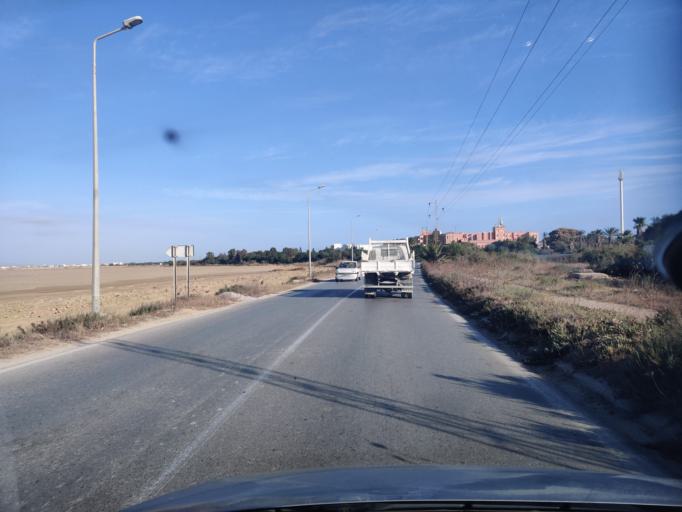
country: TN
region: Tunis
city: Al Marsa
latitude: 36.9363
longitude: 10.2531
